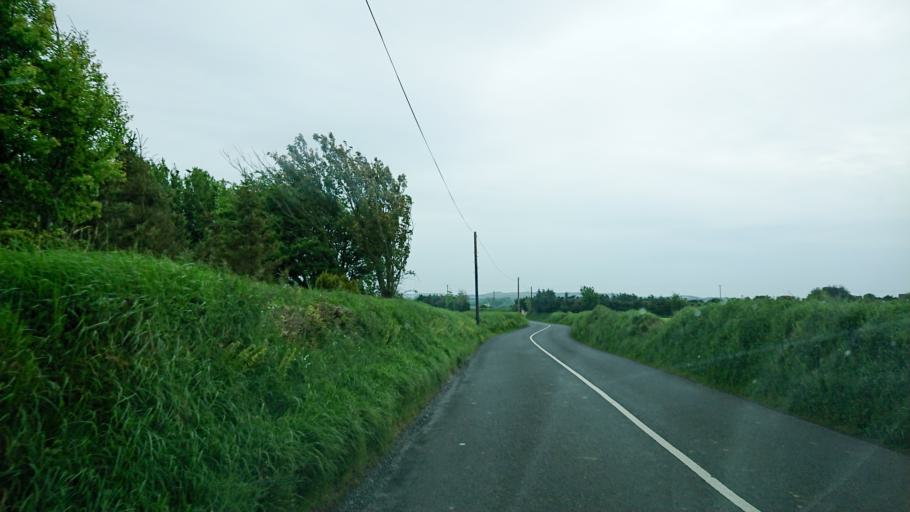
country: IE
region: Munster
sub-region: Waterford
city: Waterford
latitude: 52.2230
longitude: -7.0531
